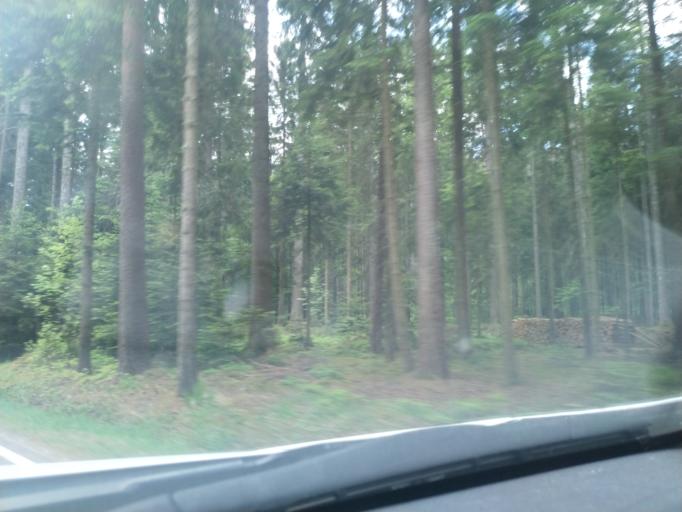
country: DE
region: Baden-Wuerttemberg
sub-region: Karlsruhe Region
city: Baiersbronn
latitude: 48.5780
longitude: 8.4228
